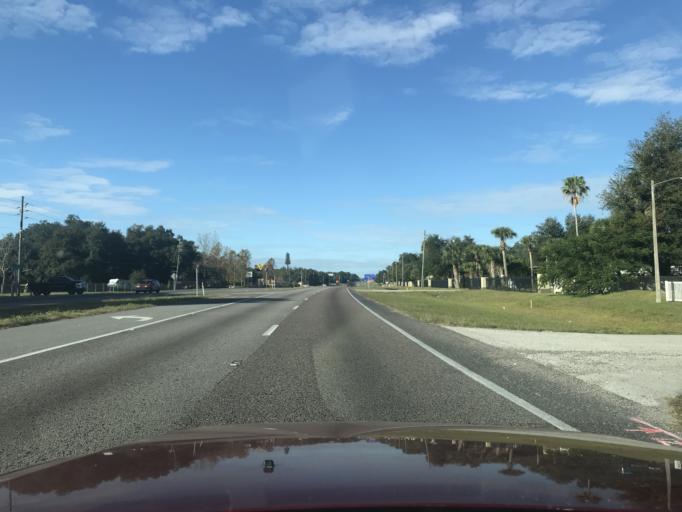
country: US
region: Florida
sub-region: Osceola County
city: Campbell
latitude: 28.2591
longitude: -81.4409
